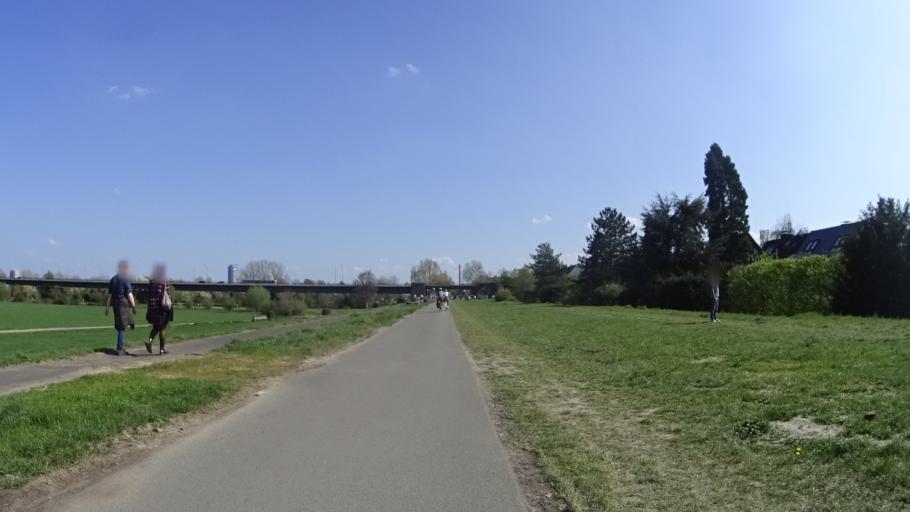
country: DE
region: North Rhine-Westphalia
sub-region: Regierungsbezirk Dusseldorf
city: Dusseldorf
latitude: 51.2444
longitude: 6.7494
